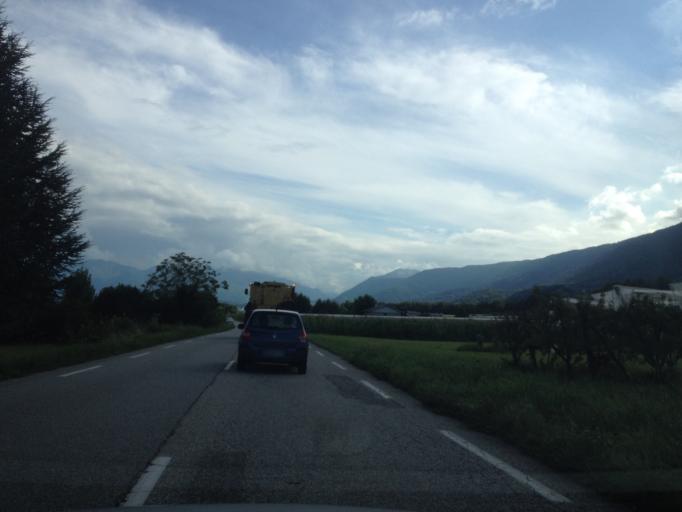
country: FR
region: Rhone-Alpes
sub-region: Departement de la Savoie
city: Le Bourget-du-Lac
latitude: 45.6302
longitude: 5.8626
